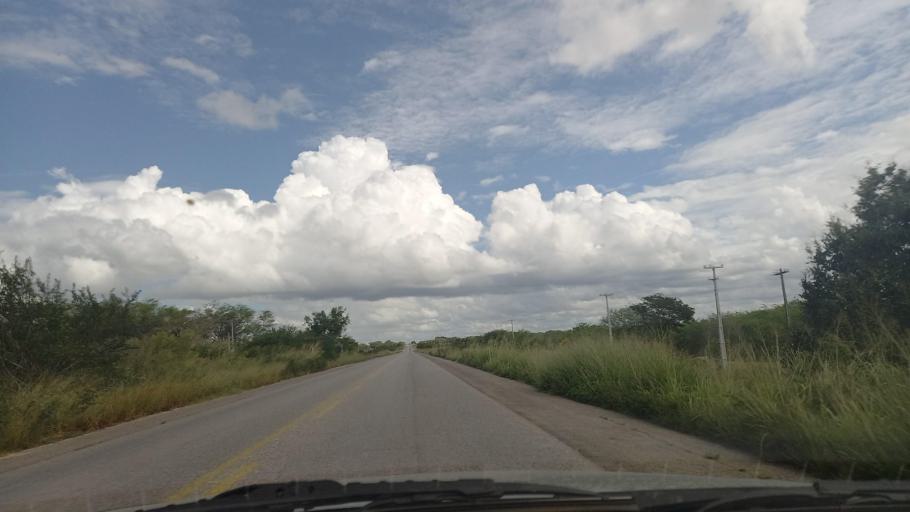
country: BR
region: Pernambuco
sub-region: Cachoeirinha
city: Cachoeirinha
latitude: -8.4503
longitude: -36.2110
